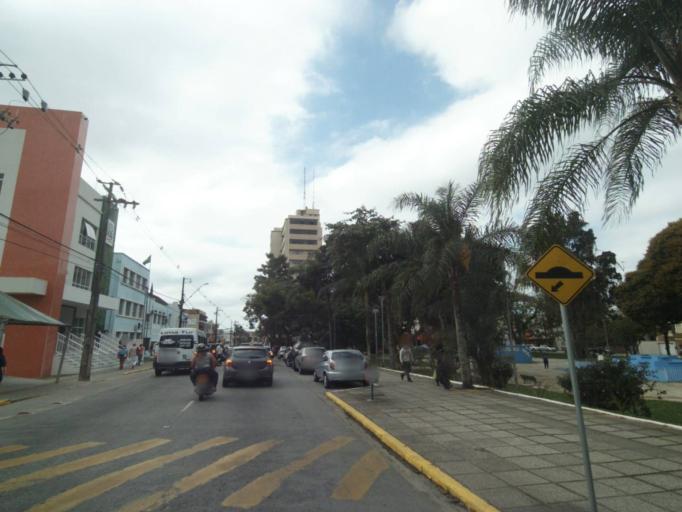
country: BR
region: Parana
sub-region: Paranagua
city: Paranagua
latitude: -25.5194
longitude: -48.5092
